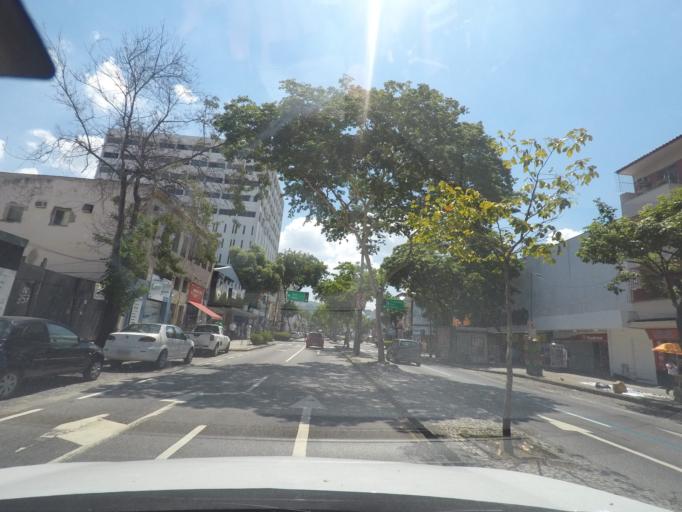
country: BR
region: Rio de Janeiro
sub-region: Rio De Janeiro
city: Rio de Janeiro
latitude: -22.9160
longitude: -43.2471
